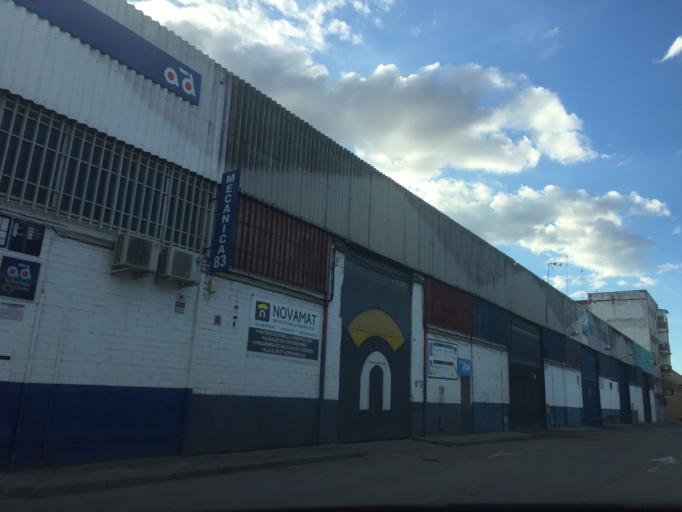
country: ES
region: Andalusia
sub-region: Provincia de Sevilla
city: Sevilla
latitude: 37.3652
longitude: -5.9603
